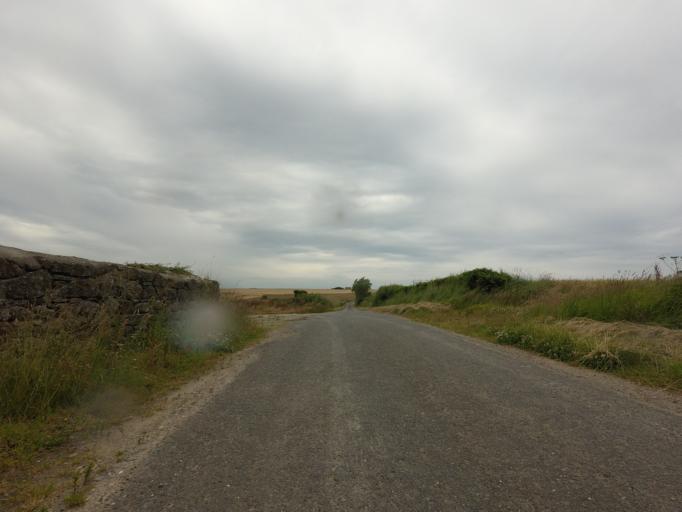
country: GB
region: Scotland
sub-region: Aberdeenshire
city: Portsoy
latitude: 57.6767
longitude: -2.6646
